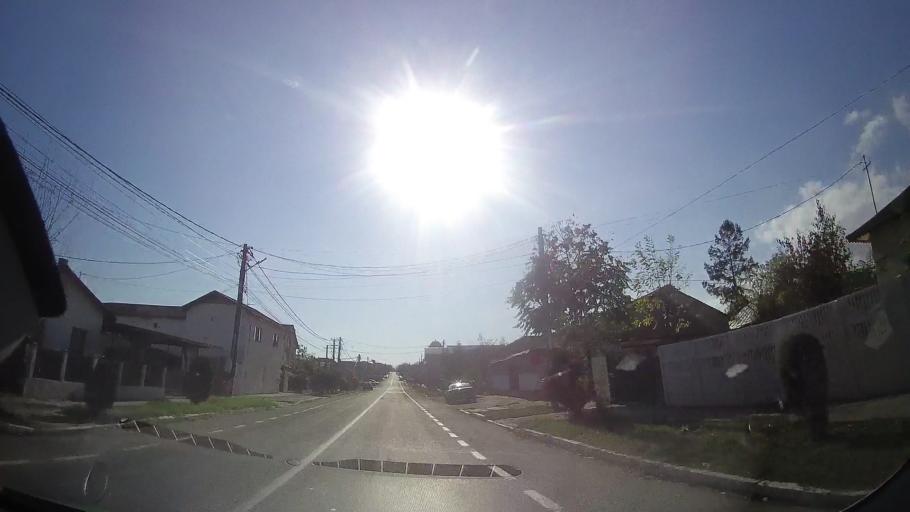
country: RO
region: Constanta
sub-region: Comuna Costinesti
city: Schitu
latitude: 43.9445
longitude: 28.6298
